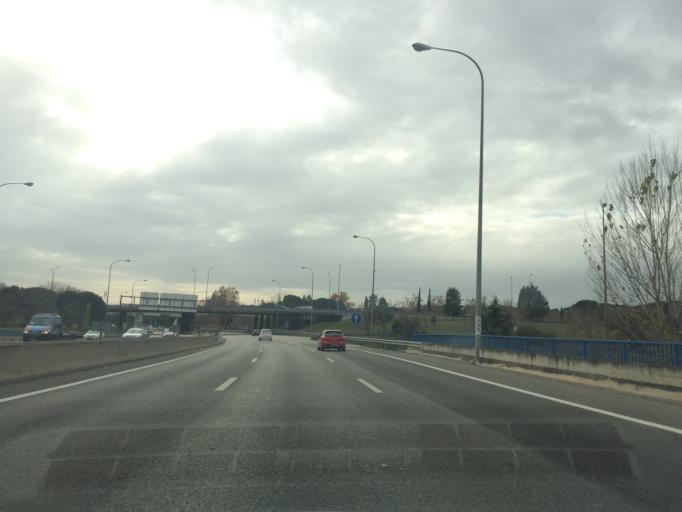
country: ES
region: Madrid
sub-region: Provincia de Madrid
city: Moncloa-Aravaca
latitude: 40.4364
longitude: -3.7382
